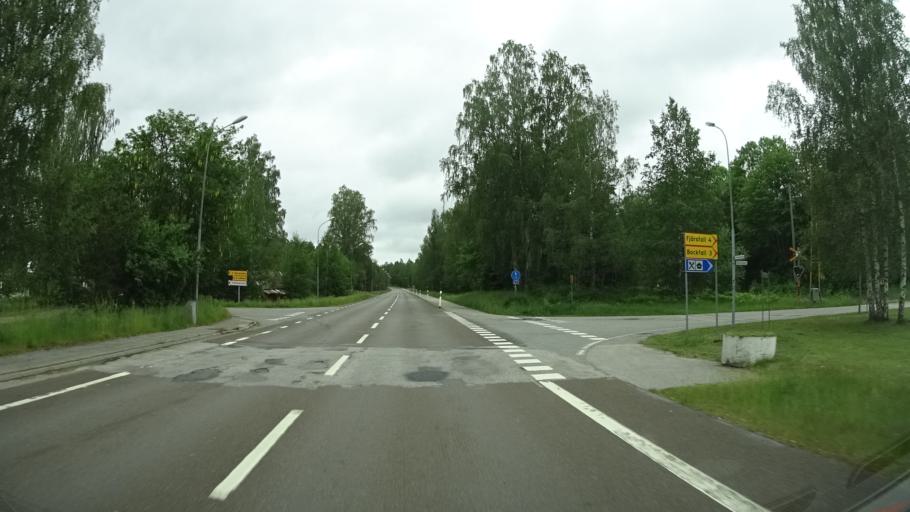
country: SE
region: Kalmar
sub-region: Hultsfreds Kommun
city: Hultsfred
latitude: 57.5510
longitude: 15.7224
